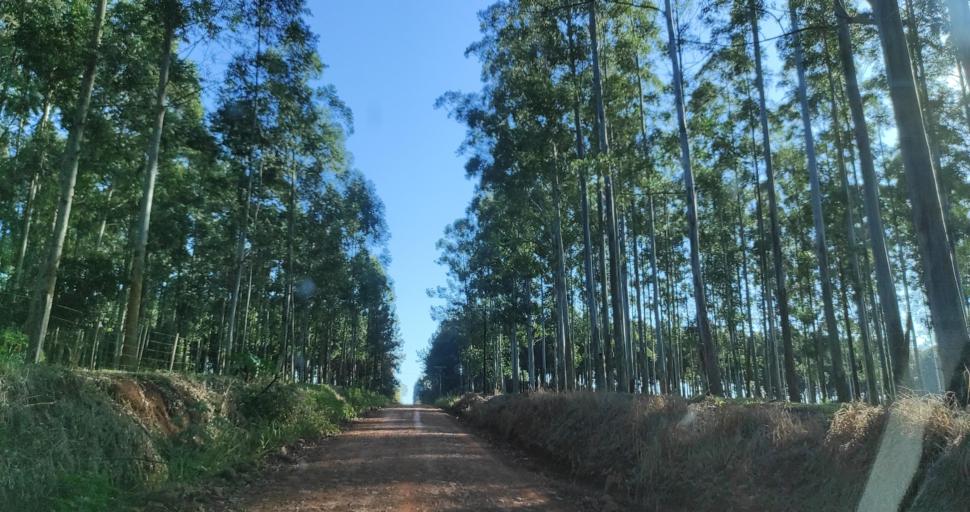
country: AR
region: Misiones
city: Puerto Rico
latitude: -26.8633
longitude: -55.0149
